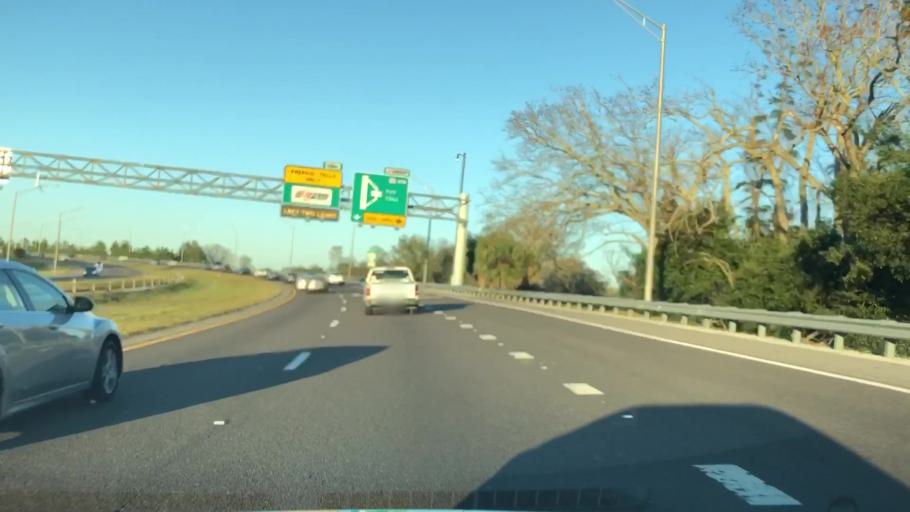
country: US
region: Florida
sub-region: Orange County
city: Paradise Heights
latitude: 28.6036
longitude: -81.5390
